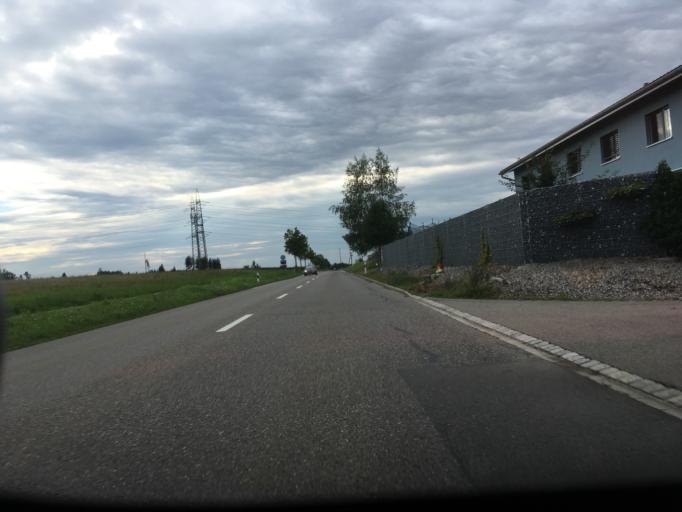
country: CH
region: Zurich
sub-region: Bezirk Pfaeffikon
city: Hittnau / Hittnau (Dorf)
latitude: 47.3680
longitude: 8.8163
